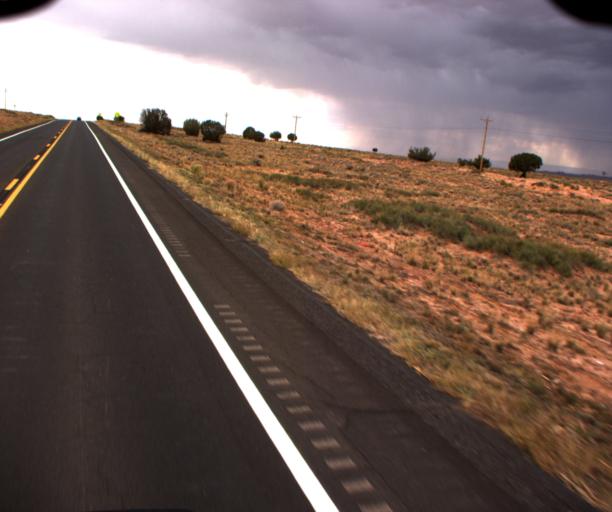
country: US
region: Arizona
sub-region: Coconino County
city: Tuba City
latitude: 36.2446
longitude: -111.0239
